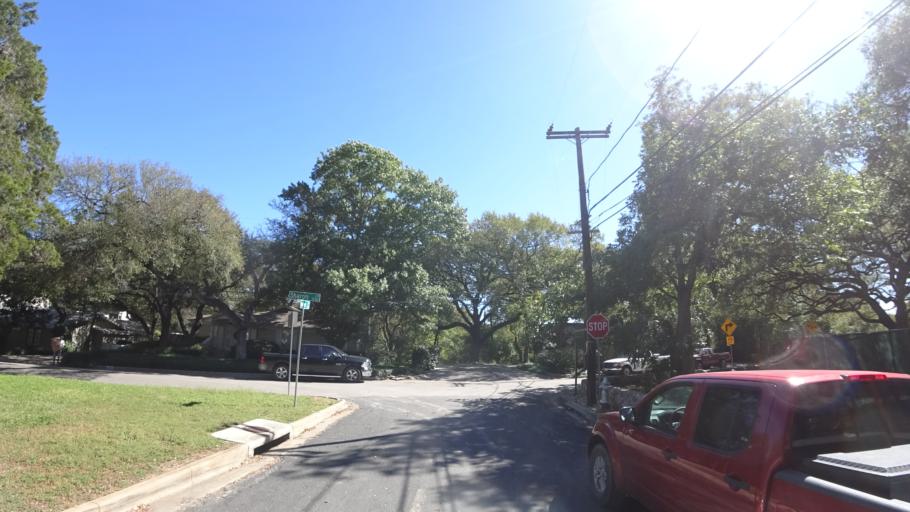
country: US
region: Texas
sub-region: Travis County
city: Rollingwood
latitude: 30.2895
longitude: -97.7642
